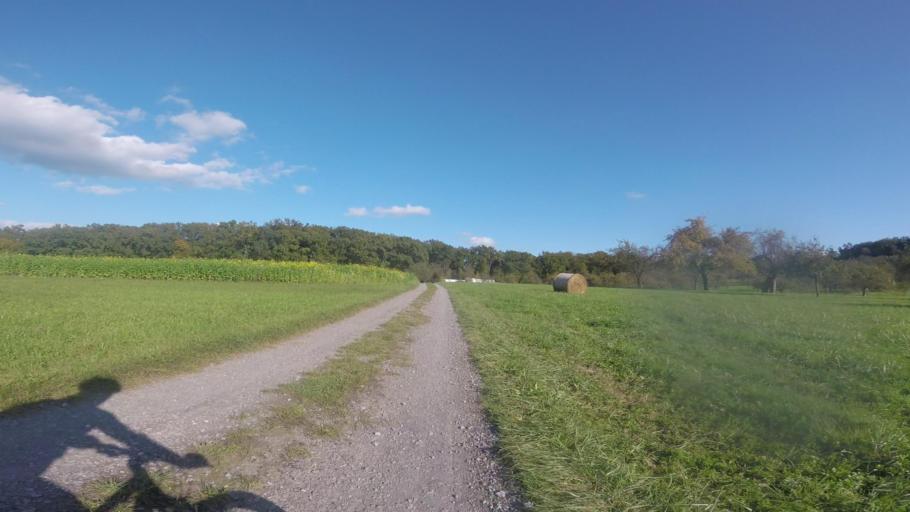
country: DE
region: Baden-Wuerttemberg
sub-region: Regierungsbezirk Stuttgart
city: Aspach
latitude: 48.9841
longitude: 9.3822
